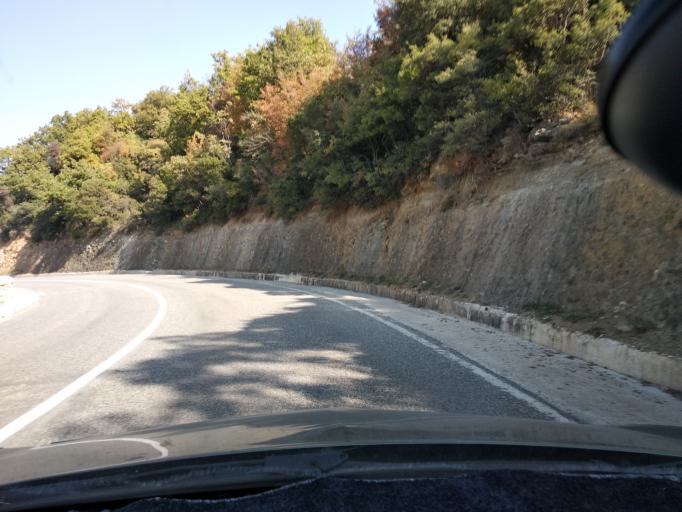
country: GR
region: Thessaly
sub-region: Trikala
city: Kalampaka
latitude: 39.7120
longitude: 21.6383
